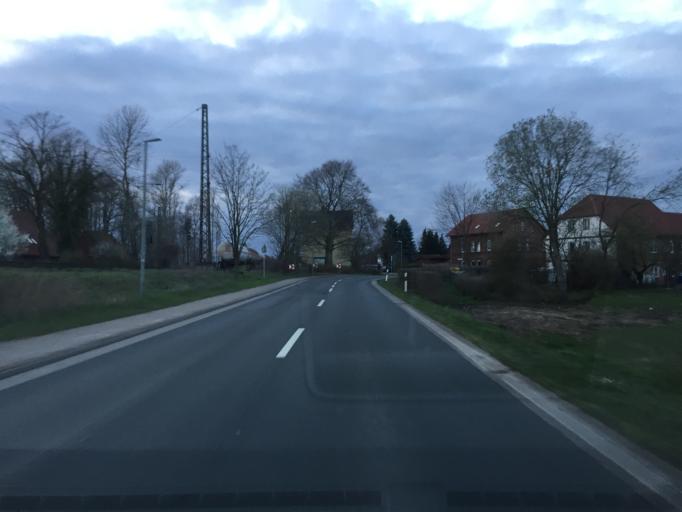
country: DE
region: Lower Saxony
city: Steimbke
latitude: 52.5767
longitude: 9.4049
